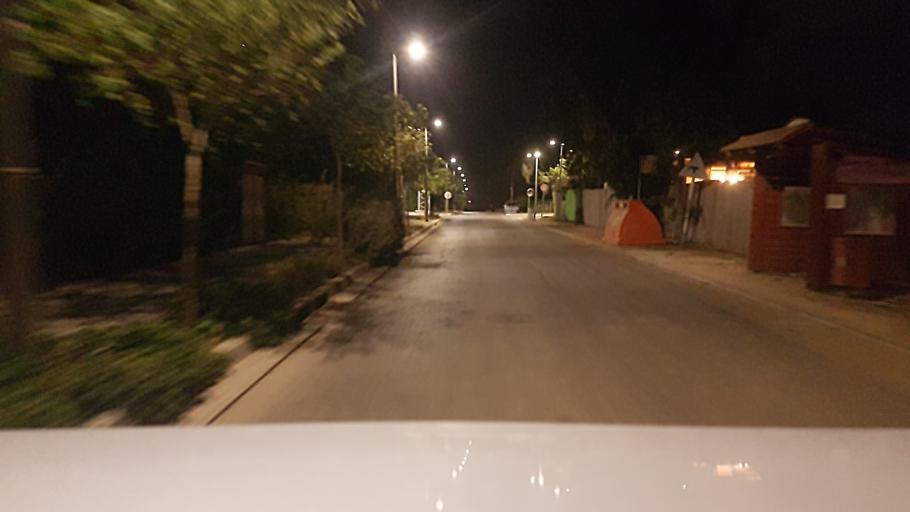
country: IL
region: Central District
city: Nehalim
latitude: 32.0751
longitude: 34.9235
